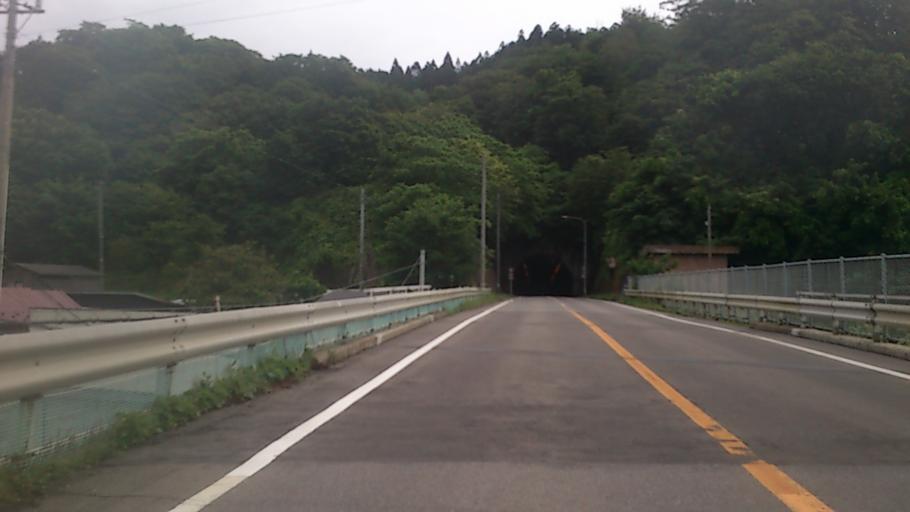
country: JP
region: Akita
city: Noshiromachi
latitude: 40.4862
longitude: 139.9495
